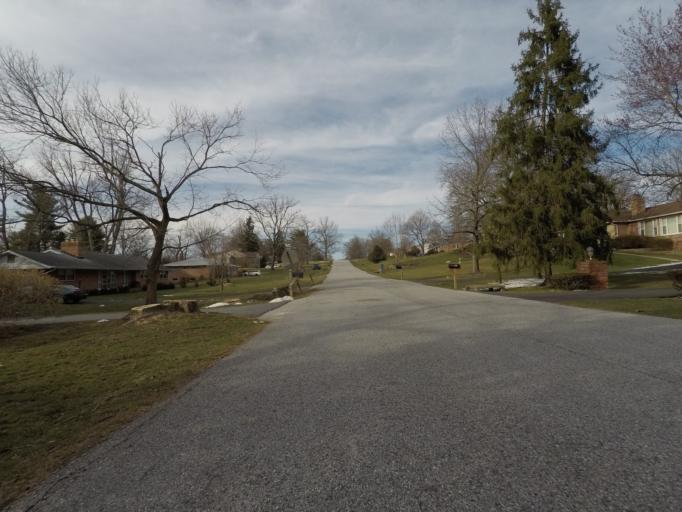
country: US
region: Maryland
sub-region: Howard County
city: Columbia
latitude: 39.2580
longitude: -76.8289
